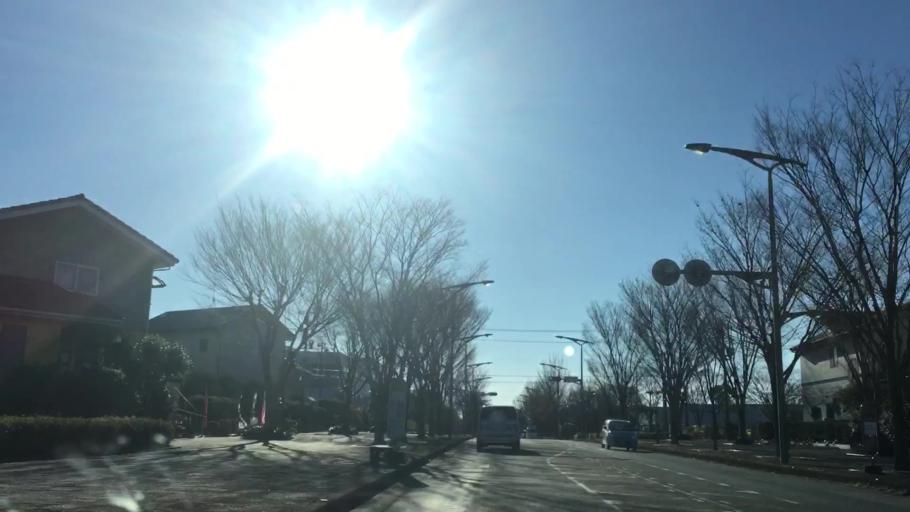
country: JP
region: Shizuoka
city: Hamakita
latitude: 34.8149
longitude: 137.7421
